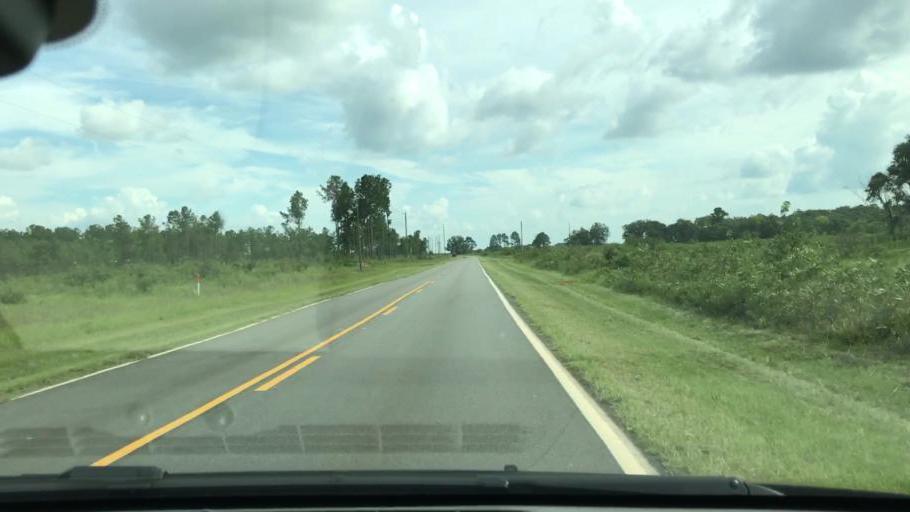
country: US
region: Georgia
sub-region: Clay County
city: Fort Gaines
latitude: 31.5441
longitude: -84.9639
